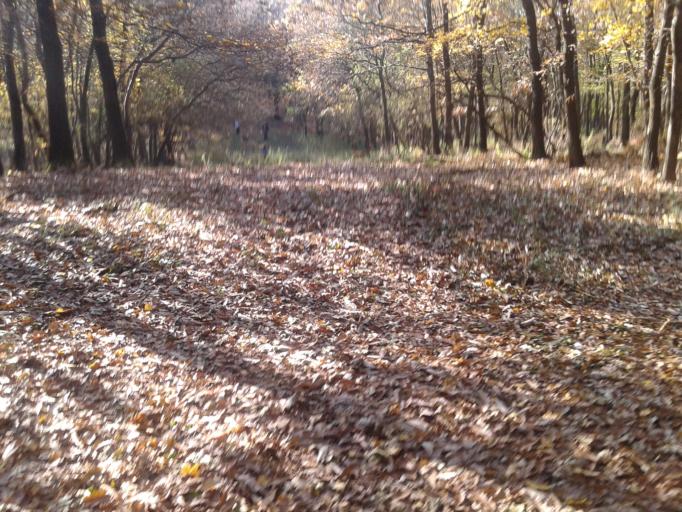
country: HU
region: Fejer
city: Bodajk
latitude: 47.3120
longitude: 18.2222
